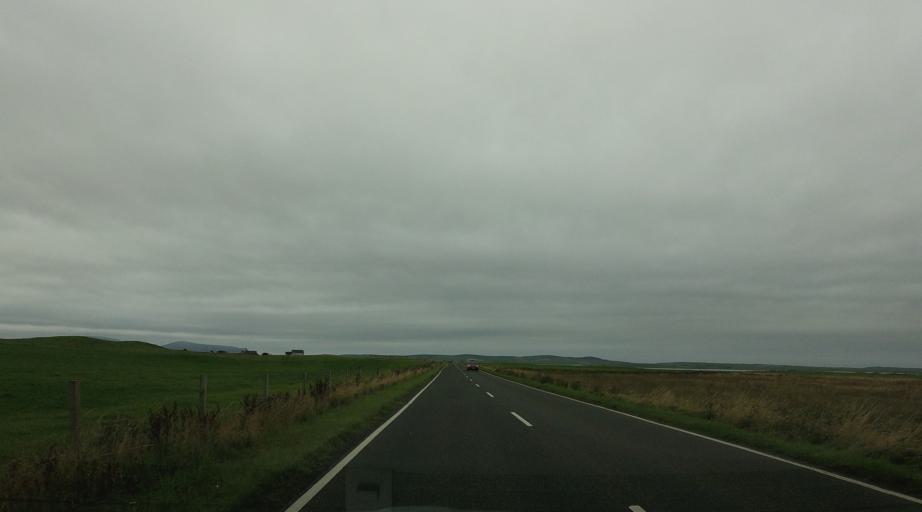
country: GB
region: Scotland
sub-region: Orkney Islands
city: Stromness
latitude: 59.0044
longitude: -3.1588
